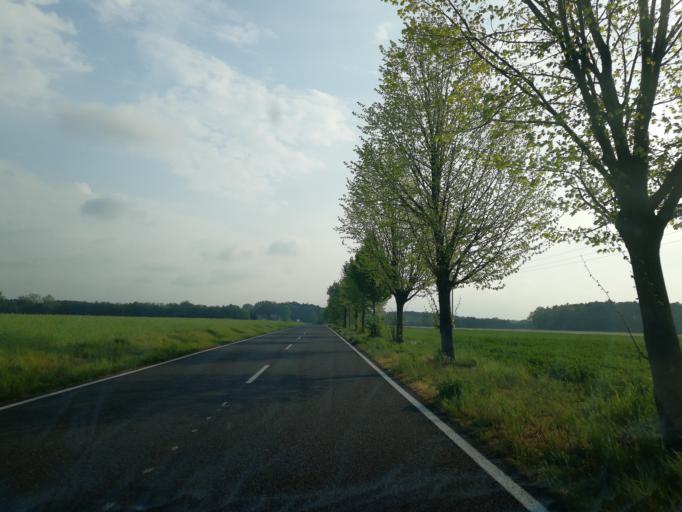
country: DE
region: Brandenburg
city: Calau
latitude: 51.7526
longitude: 13.9801
